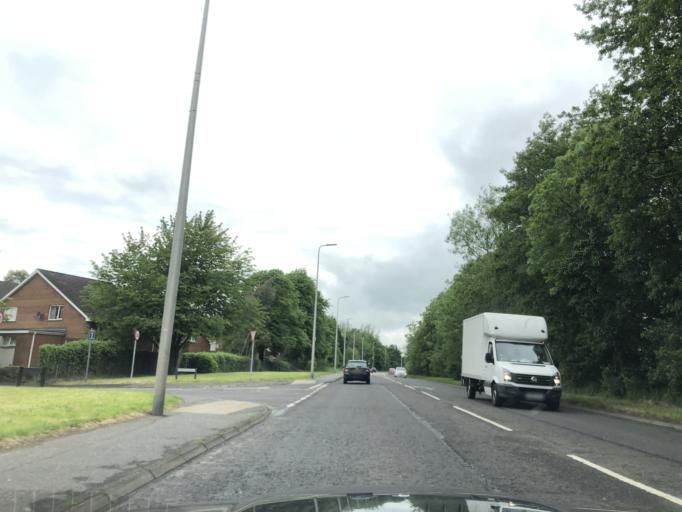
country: GB
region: Northern Ireland
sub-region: Lisburn District
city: Lisburn
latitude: 54.5164
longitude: -6.0643
